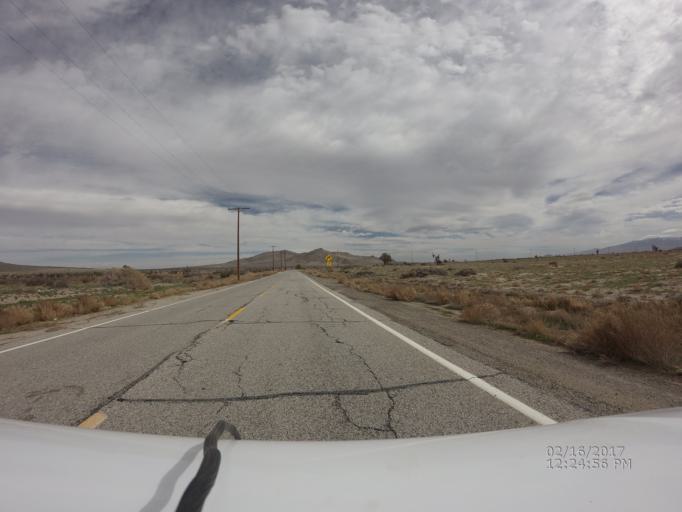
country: US
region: California
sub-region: Los Angeles County
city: Lake Los Angeles
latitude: 34.6754
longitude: -117.8478
